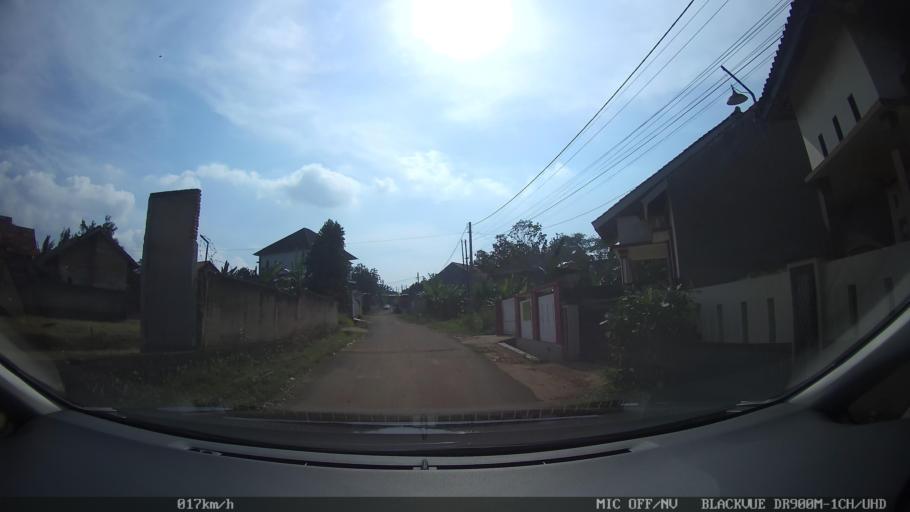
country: ID
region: Lampung
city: Kedaton
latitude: -5.3827
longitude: 105.2295
